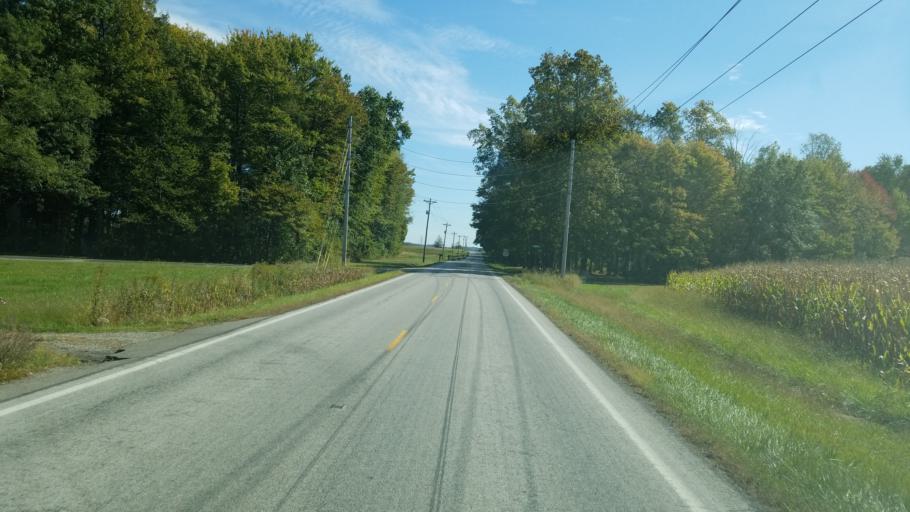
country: US
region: Ohio
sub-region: Wayne County
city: West Salem
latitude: 40.8719
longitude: -82.0959
